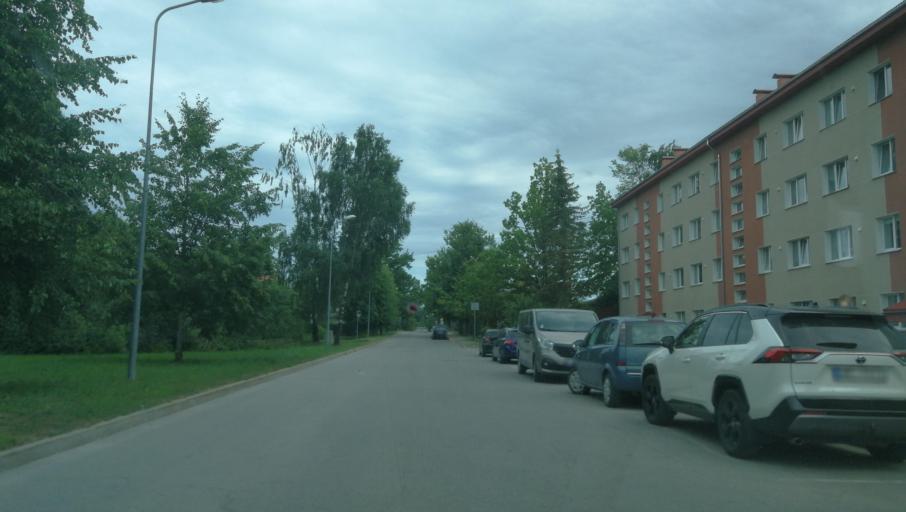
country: LV
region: Cesu Rajons
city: Cesis
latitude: 57.3035
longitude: 25.2808
